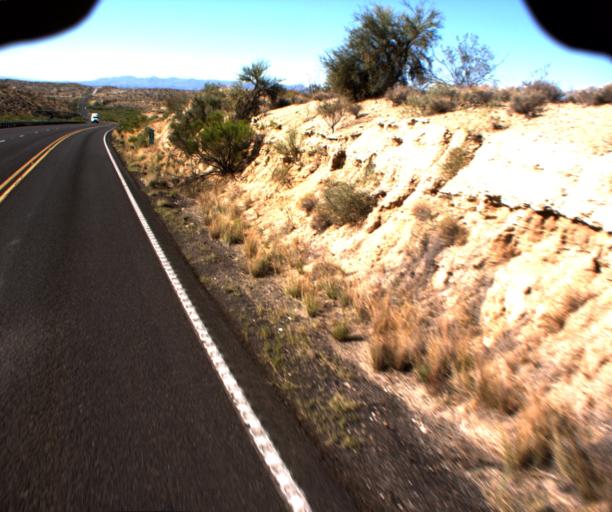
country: US
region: Arizona
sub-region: Mohave County
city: Kingman
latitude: 34.9275
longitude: -113.6588
